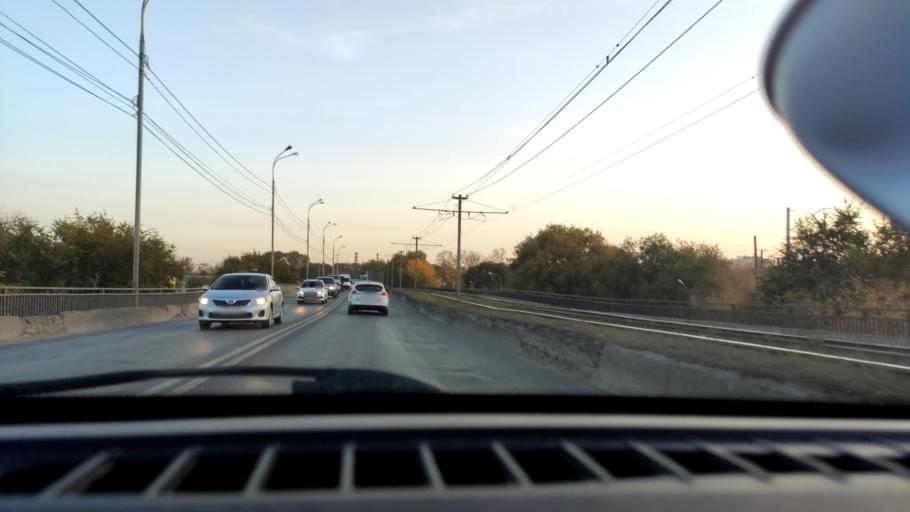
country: RU
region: Samara
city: Smyshlyayevka
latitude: 53.2190
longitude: 50.2902
